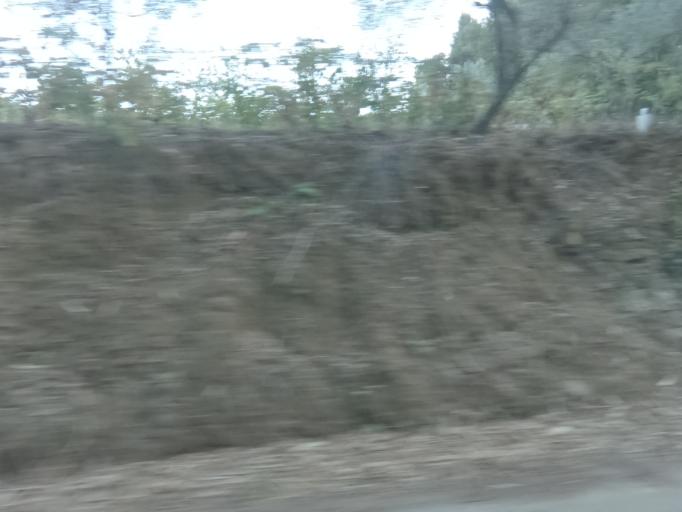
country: PT
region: Vila Real
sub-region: Mesao Frio
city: Mesao Frio
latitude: 41.1837
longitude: -7.8545
